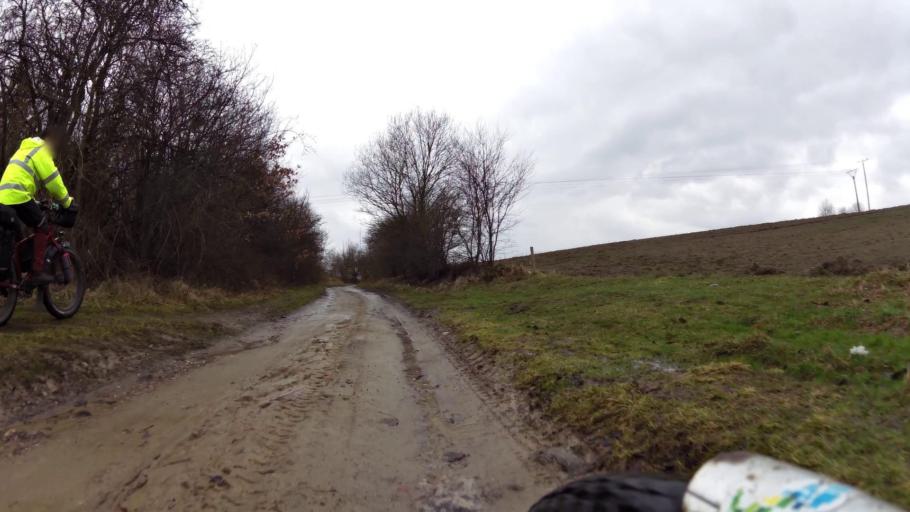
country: PL
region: Pomeranian Voivodeship
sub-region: Powiat bytowski
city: Miastko
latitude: 54.0088
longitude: 16.9911
